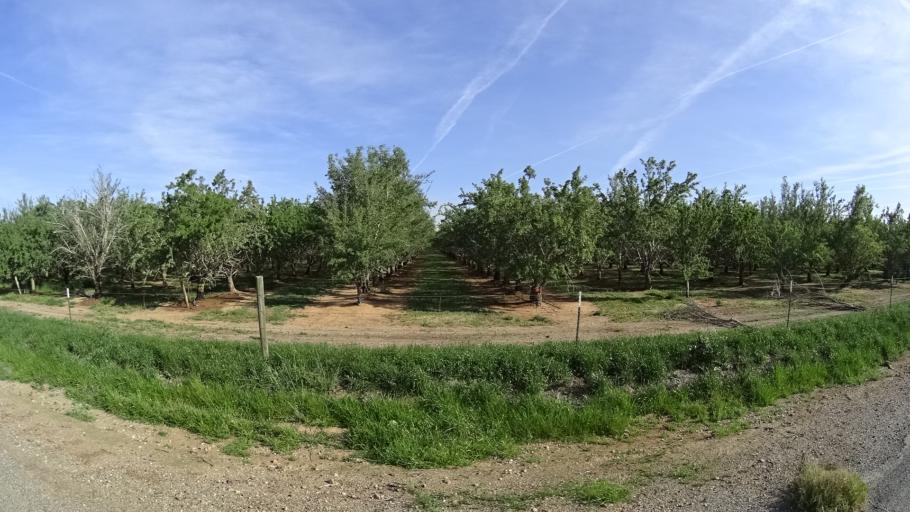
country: US
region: California
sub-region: Glenn County
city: Orland
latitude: 39.6687
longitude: -122.2887
